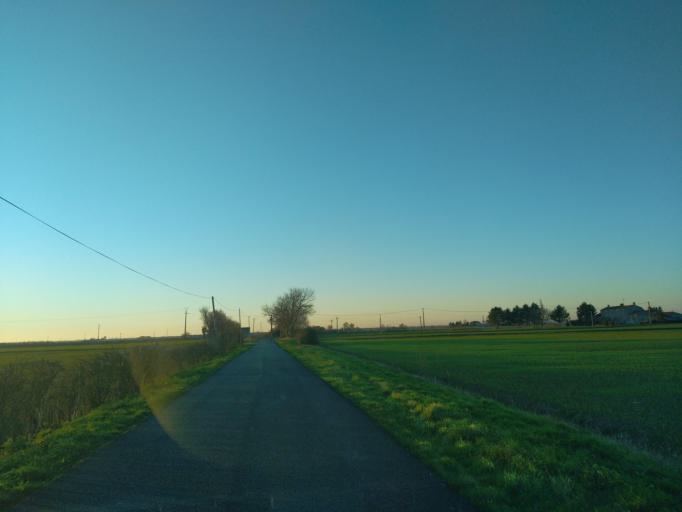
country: FR
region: Pays de la Loire
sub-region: Departement de la Vendee
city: Angles
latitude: 46.3786
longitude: -1.3110
